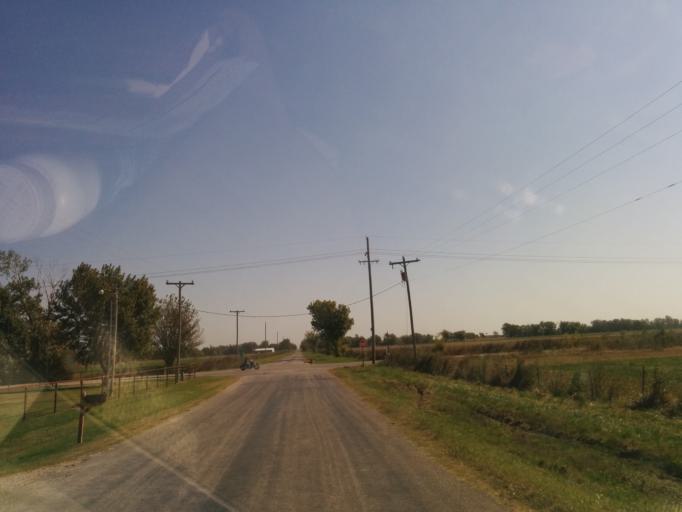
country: US
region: Oklahoma
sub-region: Okmulgee County
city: Beggs
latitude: 35.7991
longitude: -96.0696
